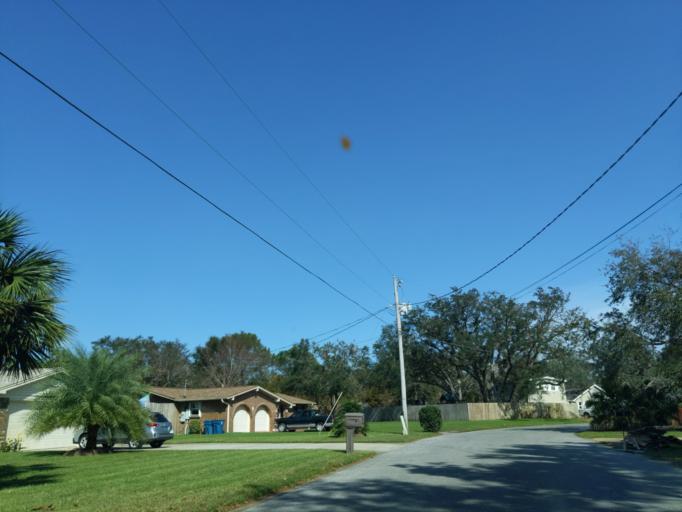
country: US
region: Florida
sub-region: Santa Rosa County
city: Gulf Breeze
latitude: 30.3597
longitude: -87.1815
